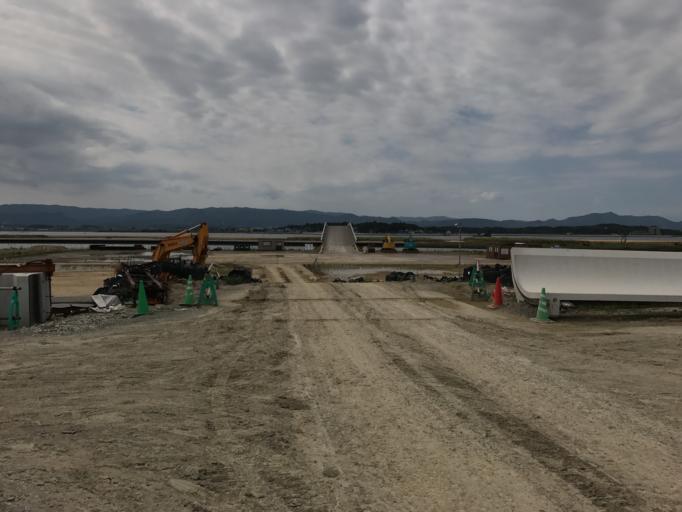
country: JP
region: Miyagi
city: Marumori
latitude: 37.8052
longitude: 140.9857
